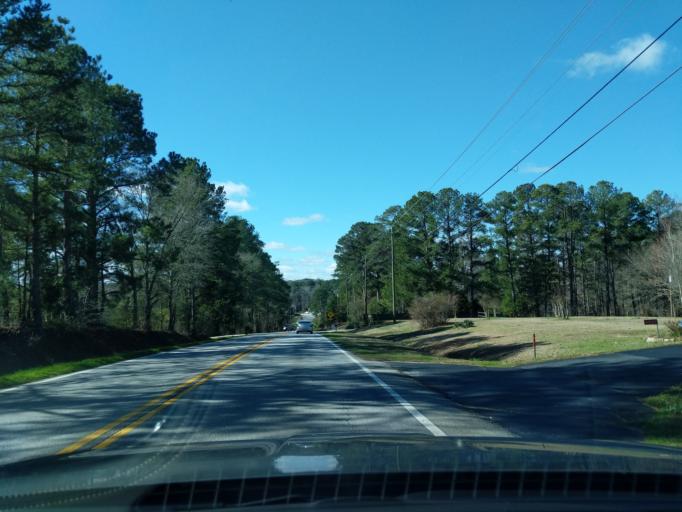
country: US
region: Georgia
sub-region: Columbia County
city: Evans
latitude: 33.5284
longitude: -82.1823
